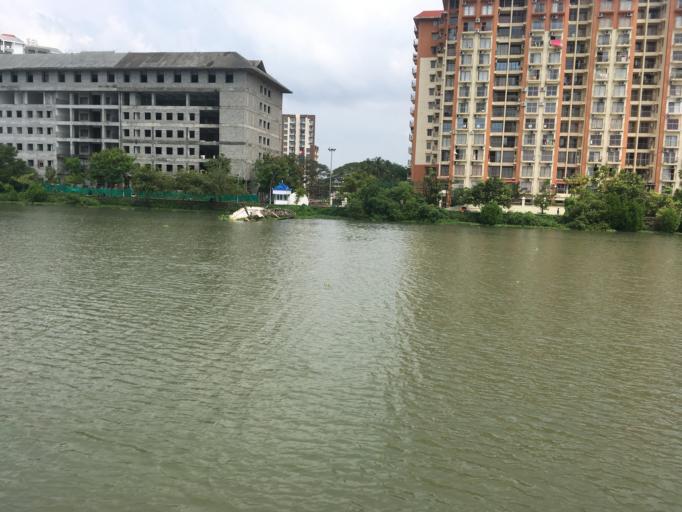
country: IN
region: Kerala
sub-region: Ernakulam
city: Cochin
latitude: 9.9875
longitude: 76.2701
